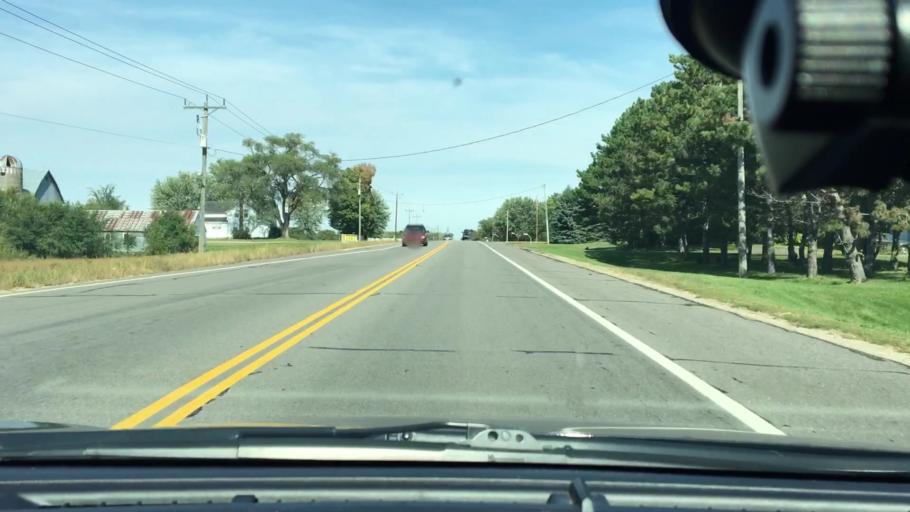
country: US
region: Minnesota
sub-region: Wright County
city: Saint Michael
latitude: 45.1909
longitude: -93.6651
